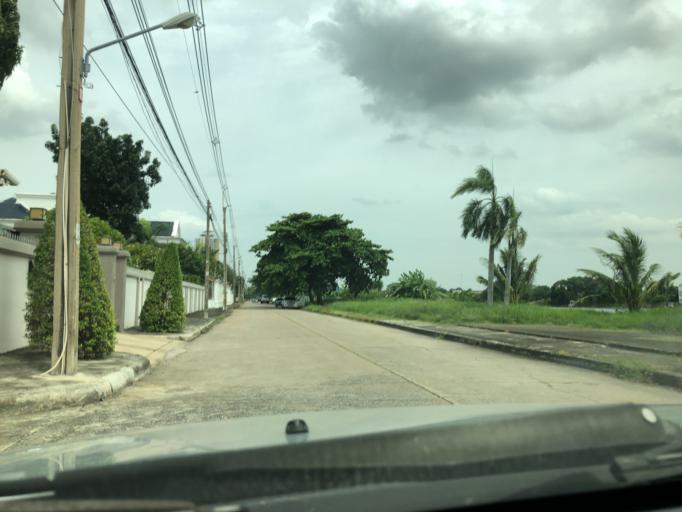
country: TH
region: Nonthaburi
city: Pak Kret
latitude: 13.9194
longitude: 100.5350
